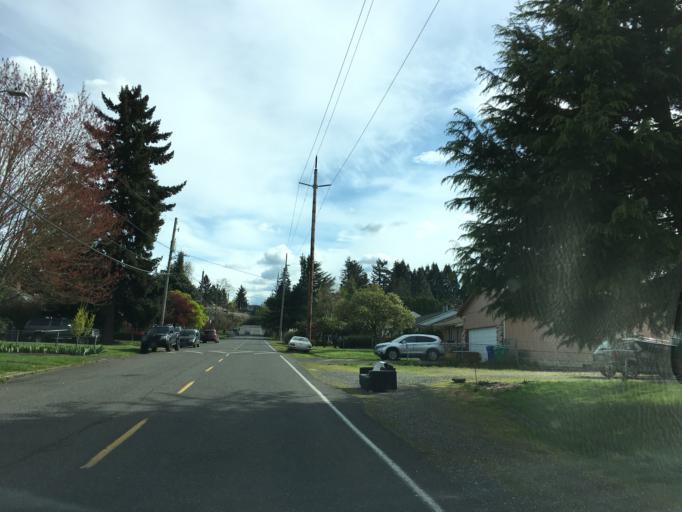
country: US
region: Oregon
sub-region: Multnomah County
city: Lents
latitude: 45.5511
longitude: -122.5475
